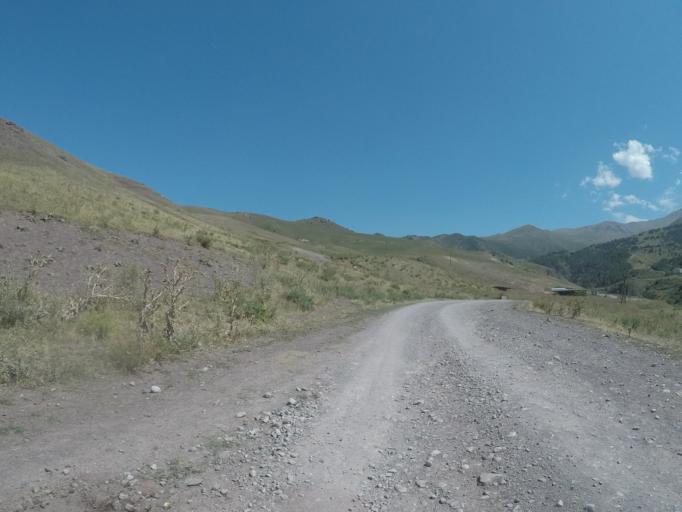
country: KG
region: Chuy
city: Bishkek
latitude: 42.6495
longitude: 74.5103
